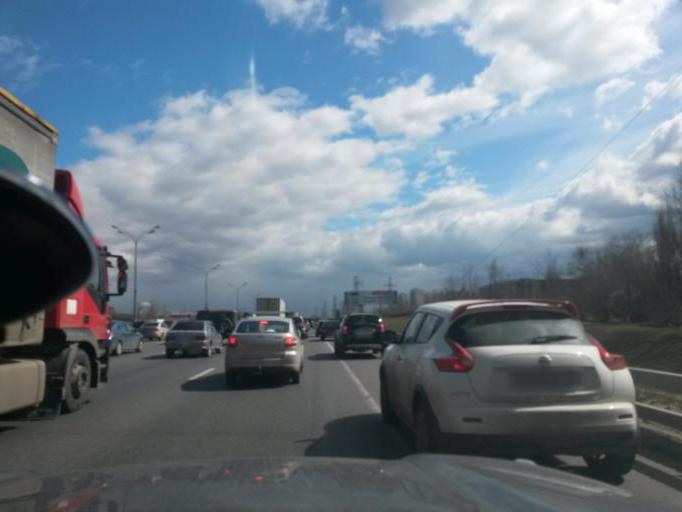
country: RU
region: Moscow
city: Chertanovo Yuzhnoye
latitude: 55.5823
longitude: 37.5665
